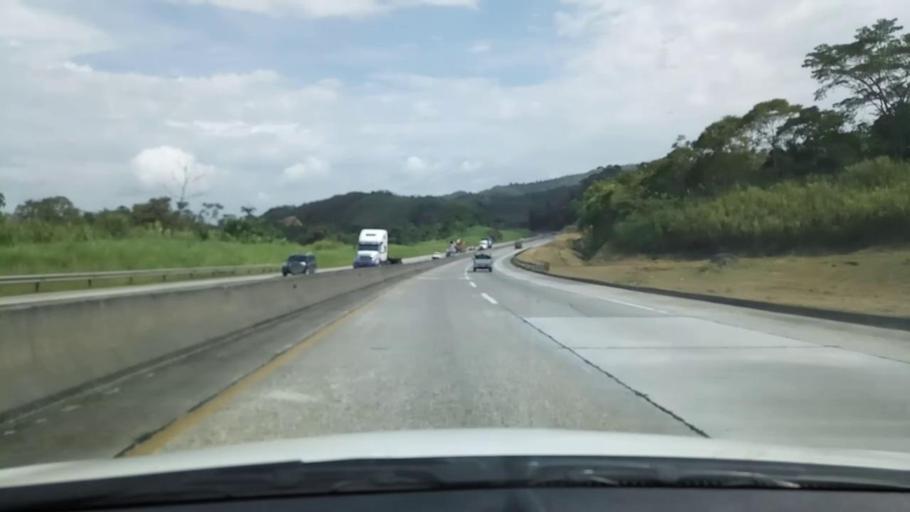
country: PA
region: Colon
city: Quebrada Bonita Adentro
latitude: 9.2797
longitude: -79.7277
